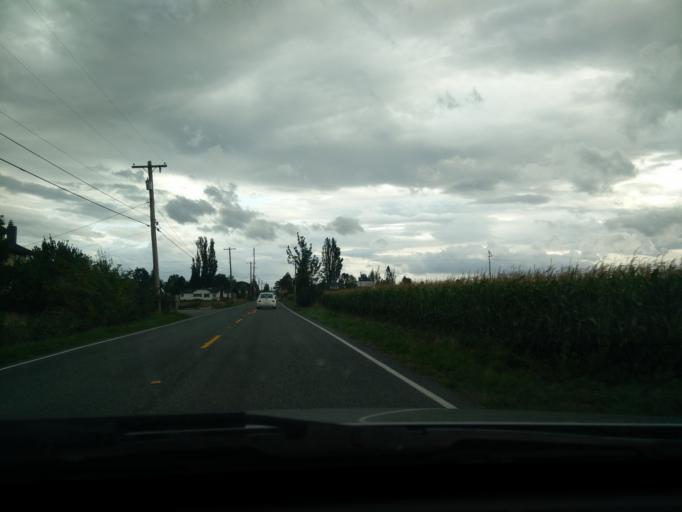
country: US
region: Washington
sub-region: Snohomish County
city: Stanwood
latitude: 48.2491
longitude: -122.3709
